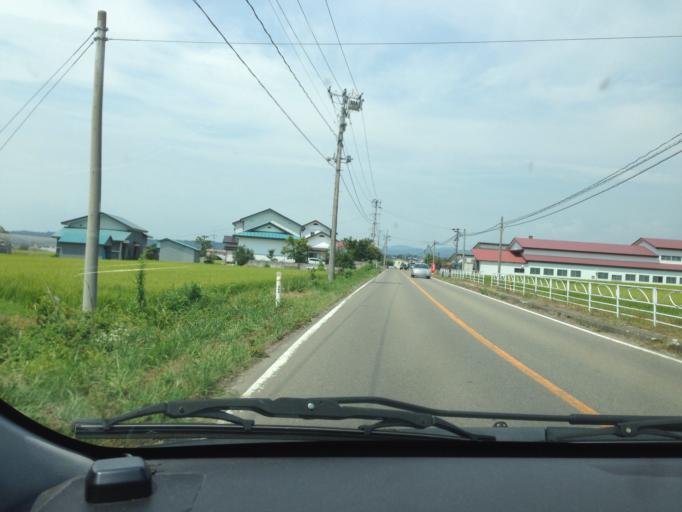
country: JP
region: Fukushima
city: Kitakata
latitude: 37.6452
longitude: 139.9059
